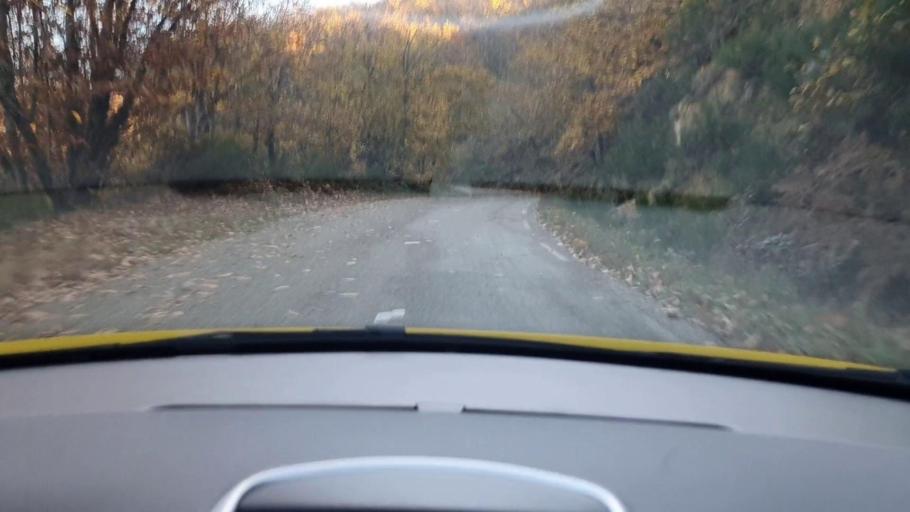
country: FR
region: Languedoc-Roussillon
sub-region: Departement du Gard
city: Lasalle
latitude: 44.0873
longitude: 3.8076
